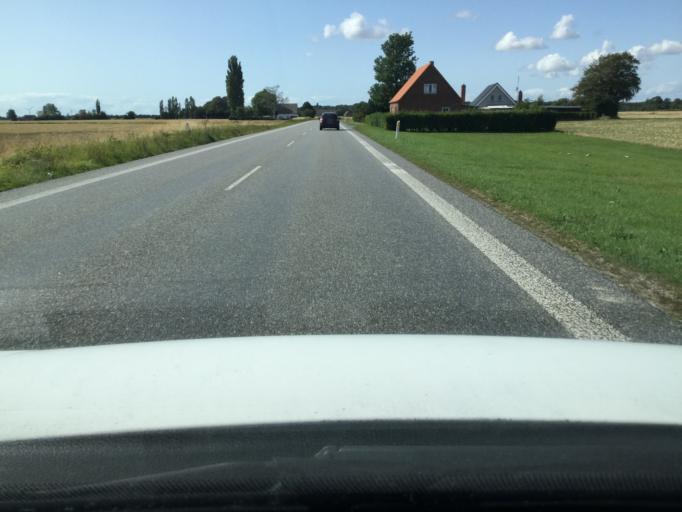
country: DK
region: Zealand
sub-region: Lolland Kommune
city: Rodby
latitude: 54.7516
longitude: 11.3748
